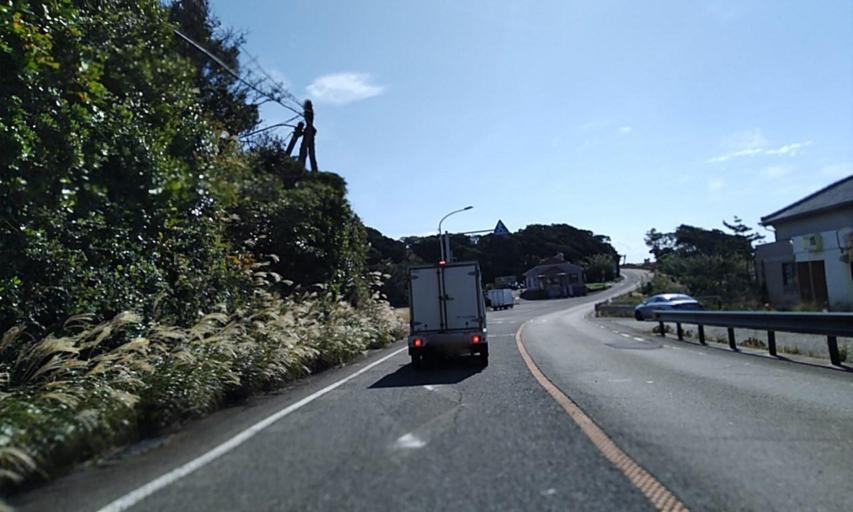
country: JP
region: Wakayama
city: Gobo
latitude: 33.7866
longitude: 135.2347
